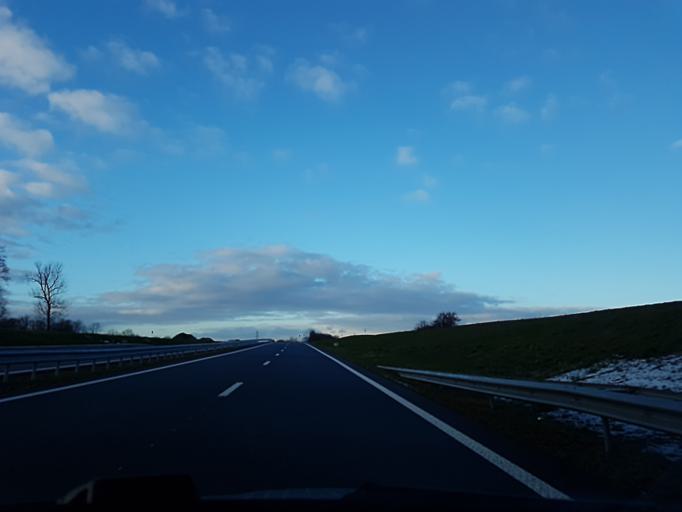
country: NL
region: Friesland
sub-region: Gemeente Tytsjerksteradiel
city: Burgum
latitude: 53.1919
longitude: 5.9774
